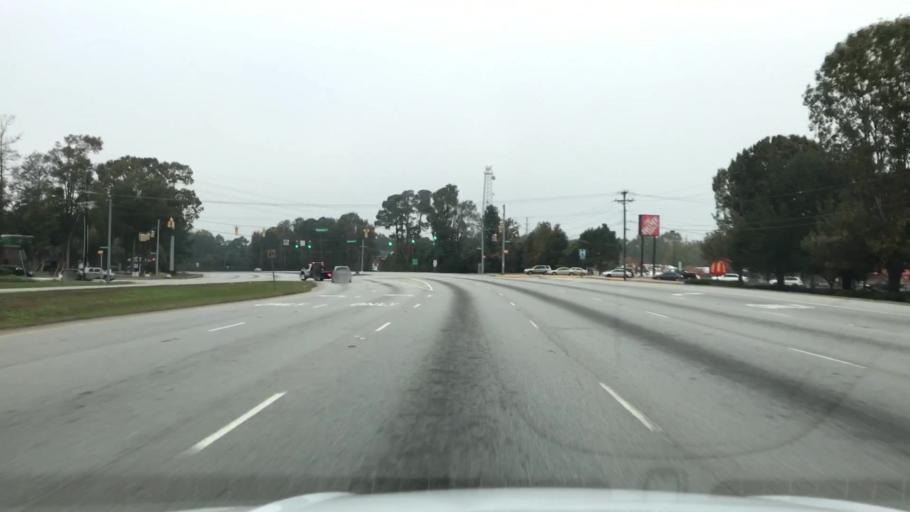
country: US
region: South Carolina
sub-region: Charleston County
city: Shell Point
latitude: 32.8119
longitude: -80.0425
